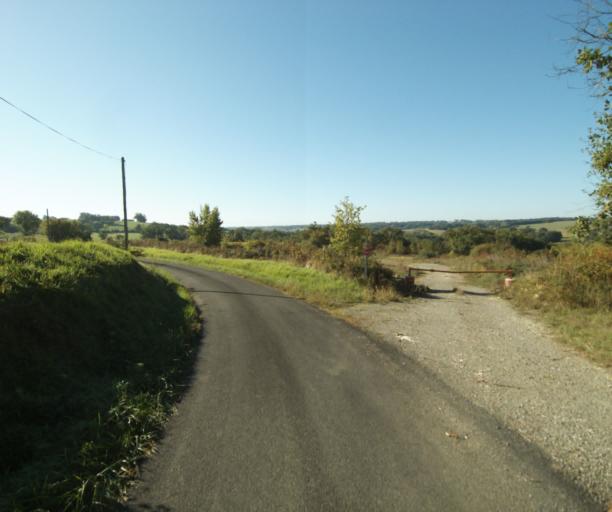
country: FR
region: Midi-Pyrenees
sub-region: Departement du Gers
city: Gondrin
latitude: 43.8275
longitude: 0.2575
